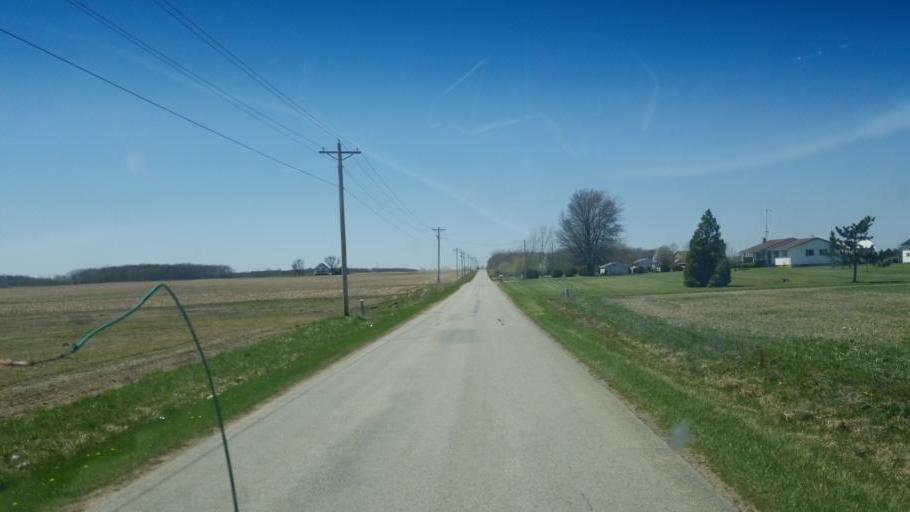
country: US
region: Ohio
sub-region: Huron County
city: Greenwich
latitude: 41.0937
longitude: -82.5063
